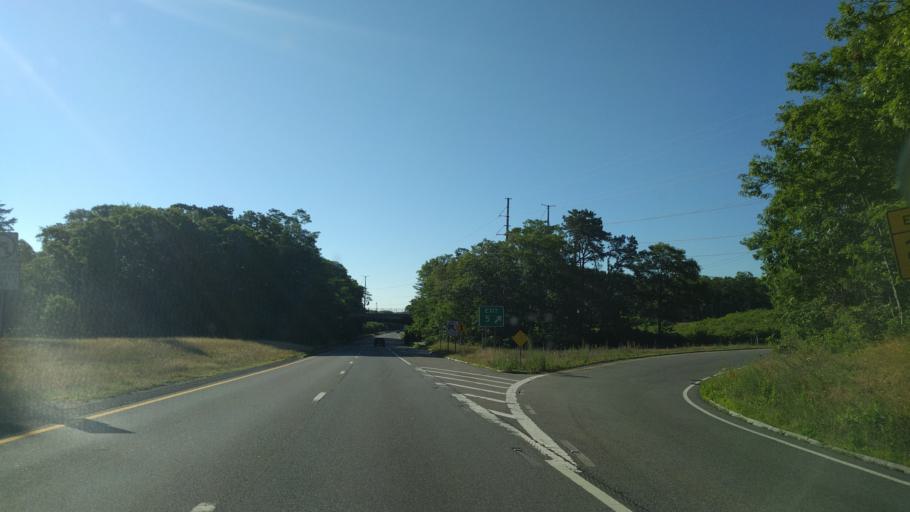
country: US
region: Massachusetts
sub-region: Barnstable County
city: West Barnstable
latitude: 41.6971
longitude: -70.3864
